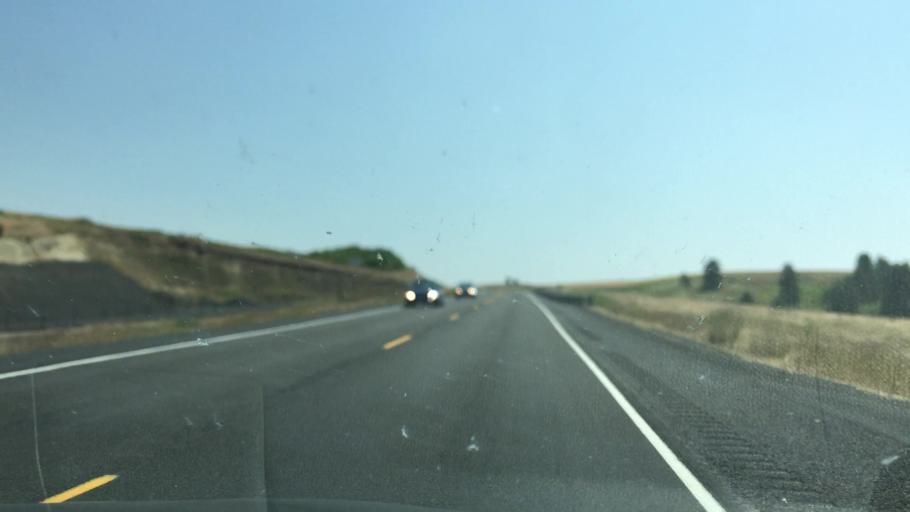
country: US
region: Idaho
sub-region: Lewis County
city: Nezperce
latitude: 46.2347
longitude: -116.5139
